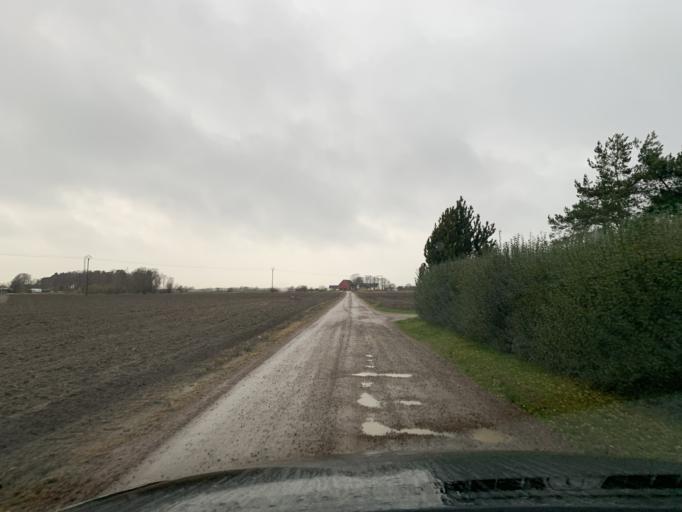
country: SE
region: Skane
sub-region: Kavlinge Kommun
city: Hofterup
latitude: 55.8391
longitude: 12.9968
